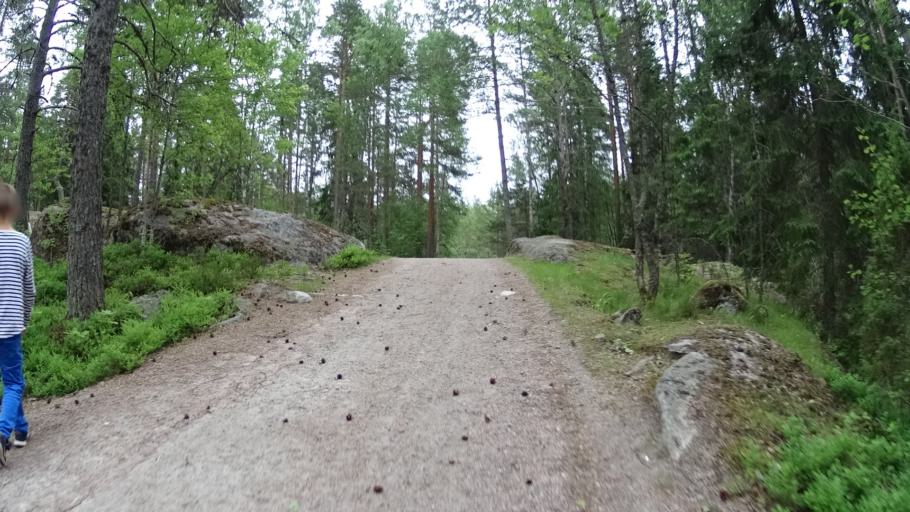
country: FI
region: Uusimaa
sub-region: Helsinki
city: Espoo
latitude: 60.2696
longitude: 24.6393
